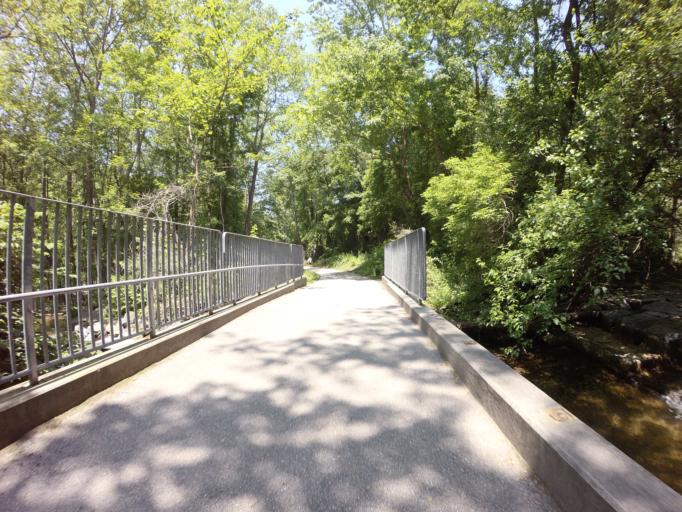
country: US
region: Maryland
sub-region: Howard County
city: Ilchester
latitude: 39.2453
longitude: -76.7523
